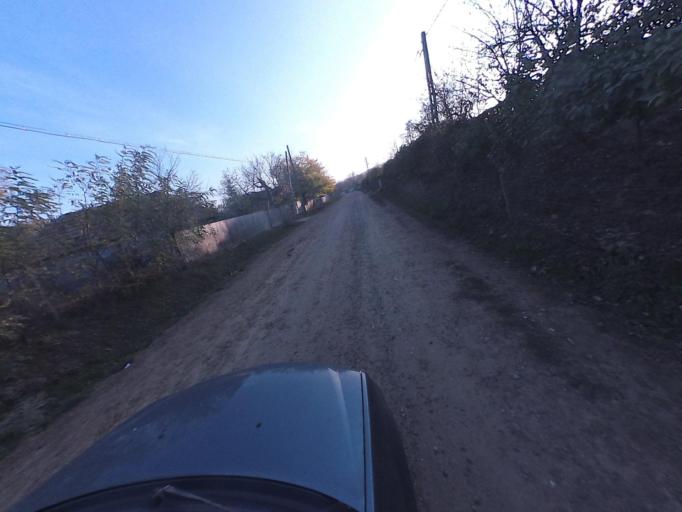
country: RO
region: Vaslui
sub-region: Comuna Bacesti
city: Bacesti
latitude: 46.8081
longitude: 27.2254
